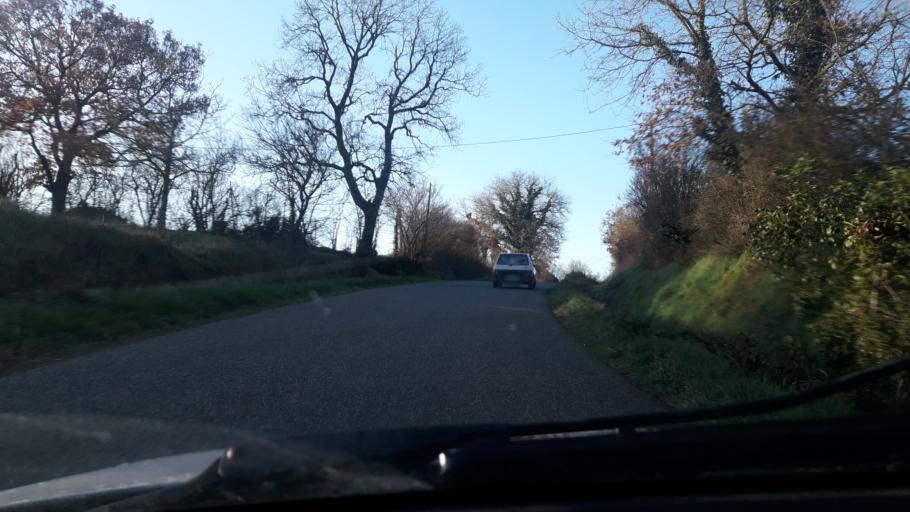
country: FR
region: Midi-Pyrenees
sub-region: Departement du Gers
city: Gimont
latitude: 43.6507
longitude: 1.0061
